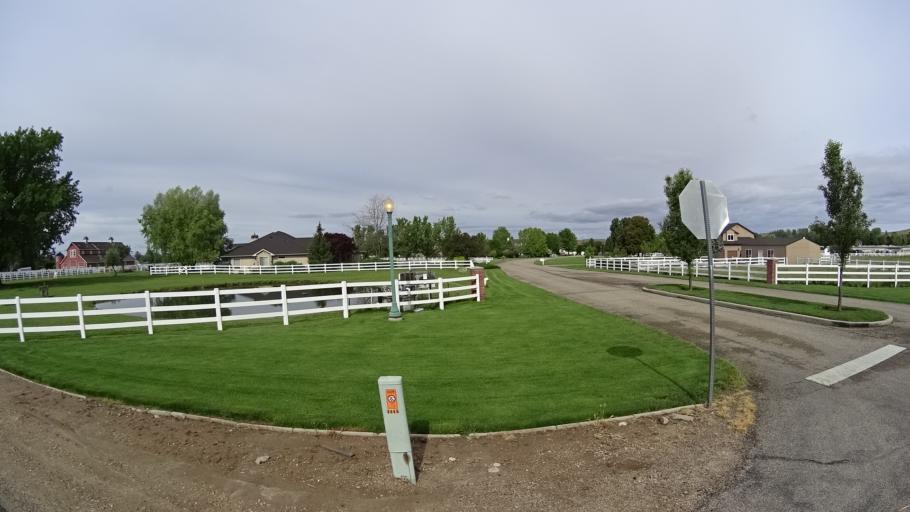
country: US
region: Idaho
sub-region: Ada County
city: Eagle
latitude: 43.7259
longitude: -116.4029
